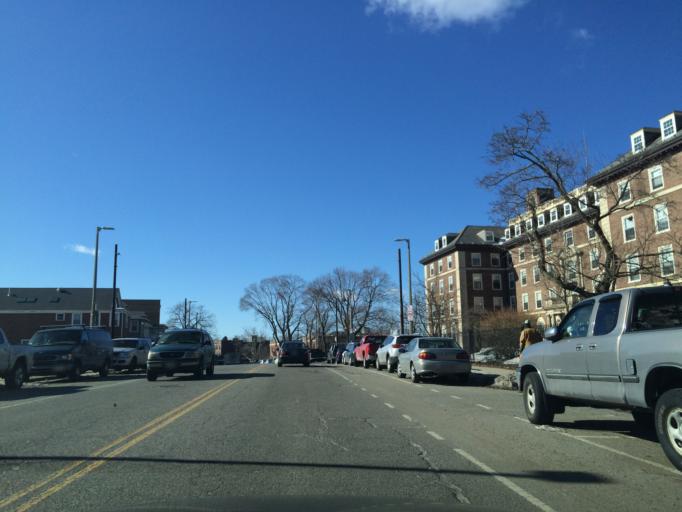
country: US
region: Massachusetts
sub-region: Norfolk County
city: Brookline
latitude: 42.3261
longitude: -71.1117
